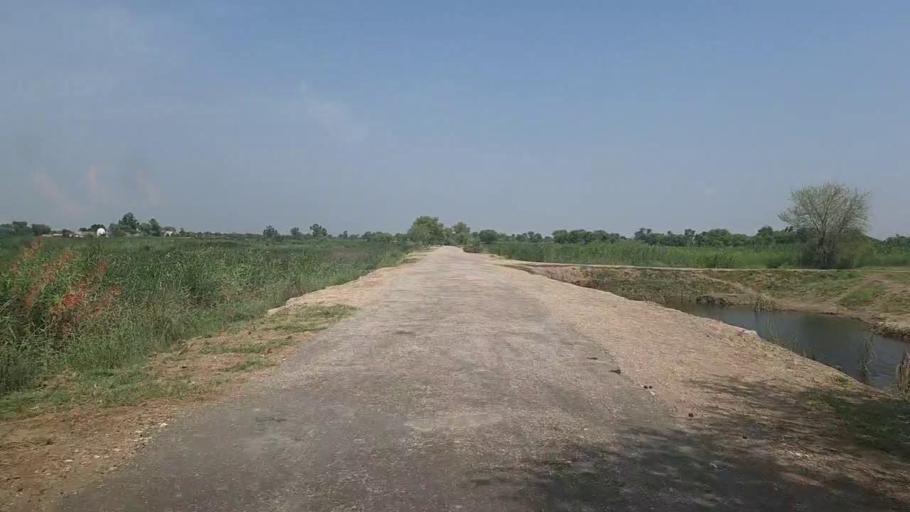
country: PK
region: Sindh
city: Ubauro
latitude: 28.1573
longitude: 69.8211
